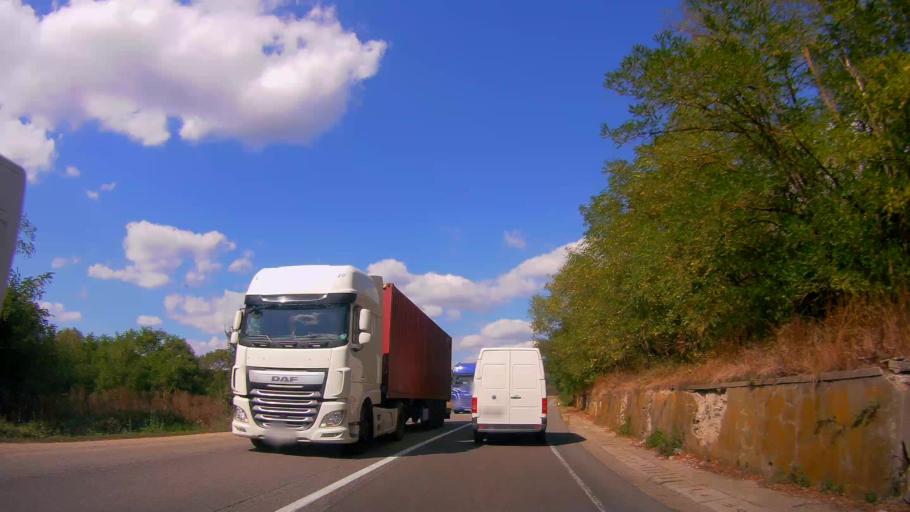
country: RO
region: Salaj
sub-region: Comuna Romanasi
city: Romanasi
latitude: 47.1115
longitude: 23.1652
